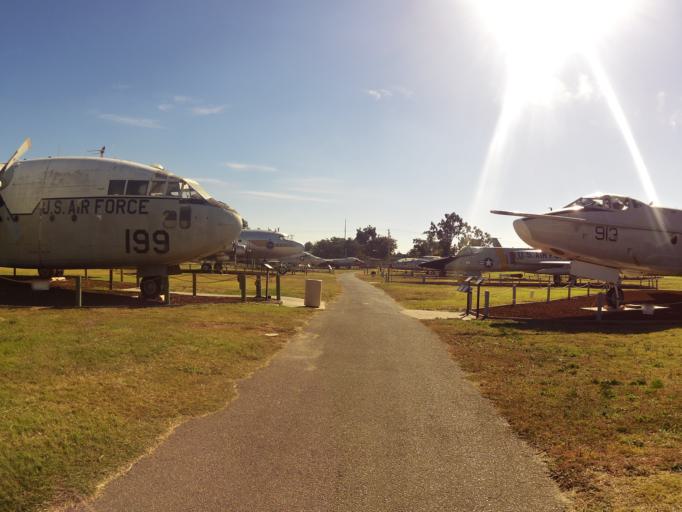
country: US
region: California
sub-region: Merced County
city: Atwater
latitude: 37.3690
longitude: -120.5783
